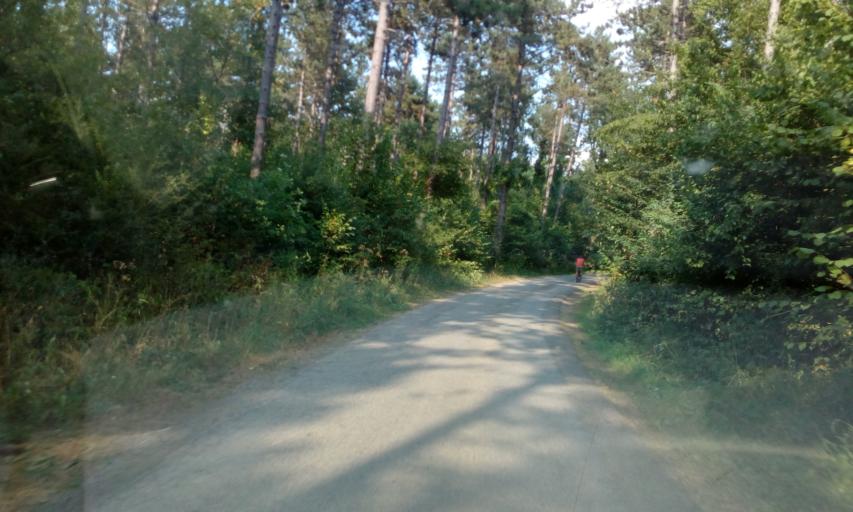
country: BE
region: Wallonia
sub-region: Province du Luxembourg
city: Tellin
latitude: 50.1104
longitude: 5.2262
